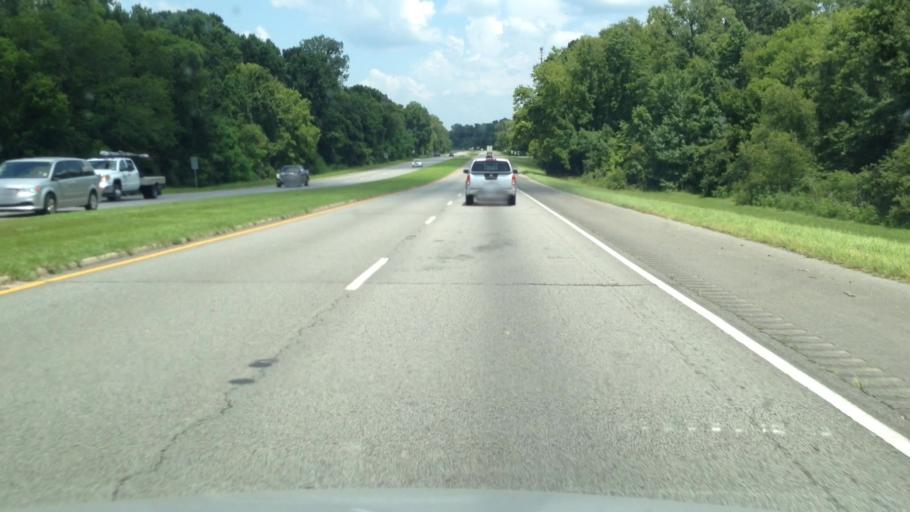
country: US
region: Louisiana
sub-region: Saint Landry Parish
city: Krotz Springs
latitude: 30.5401
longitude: -91.7765
